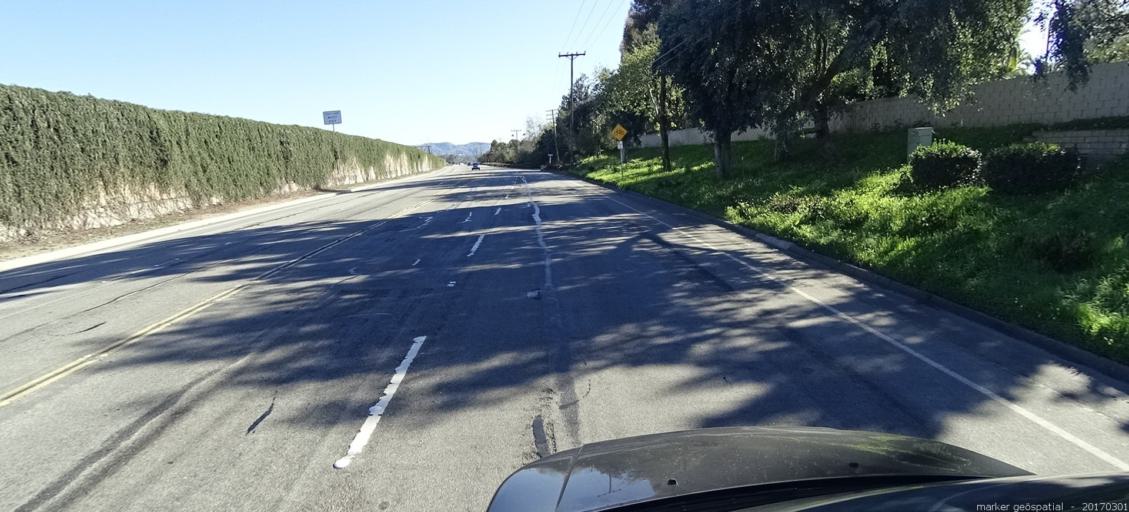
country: US
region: California
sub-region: Orange County
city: Villa Park
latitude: 33.8463
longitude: -117.8197
